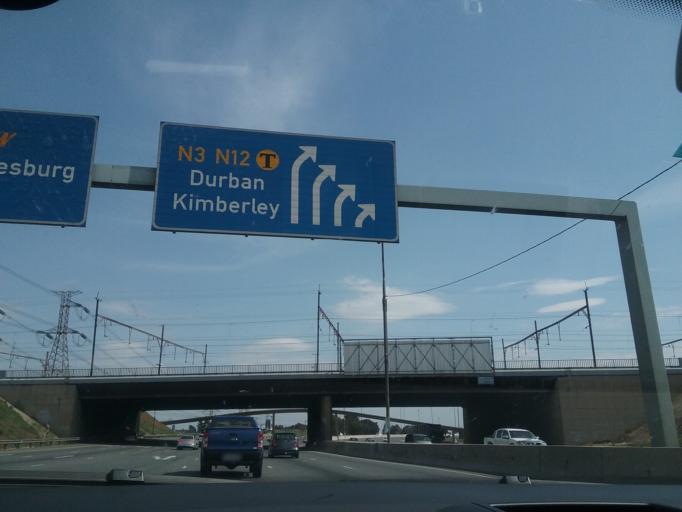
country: ZA
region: Gauteng
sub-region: Ekurhuleni Metropolitan Municipality
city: Germiston
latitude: -26.2068
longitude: 28.1366
